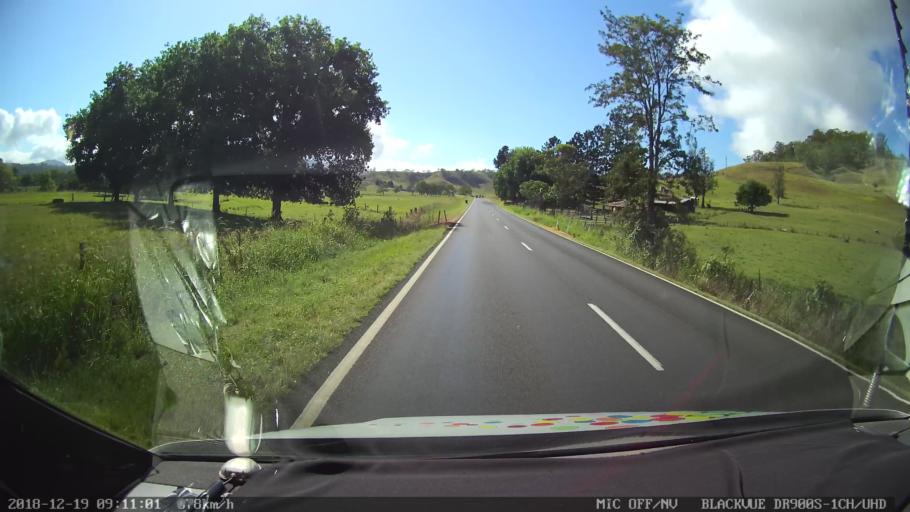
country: AU
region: New South Wales
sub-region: Kyogle
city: Kyogle
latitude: -28.4897
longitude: 152.9344
